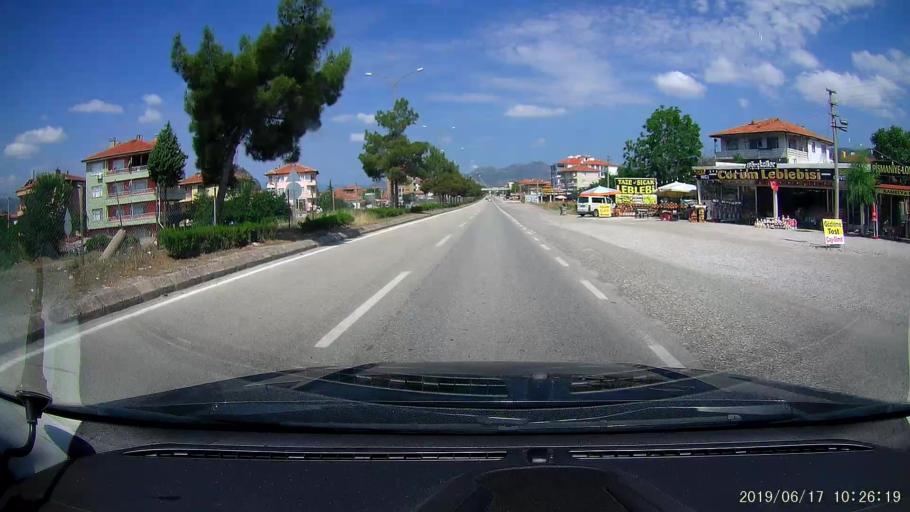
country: TR
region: Corum
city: Osmancik
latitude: 40.9728
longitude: 34.8206
